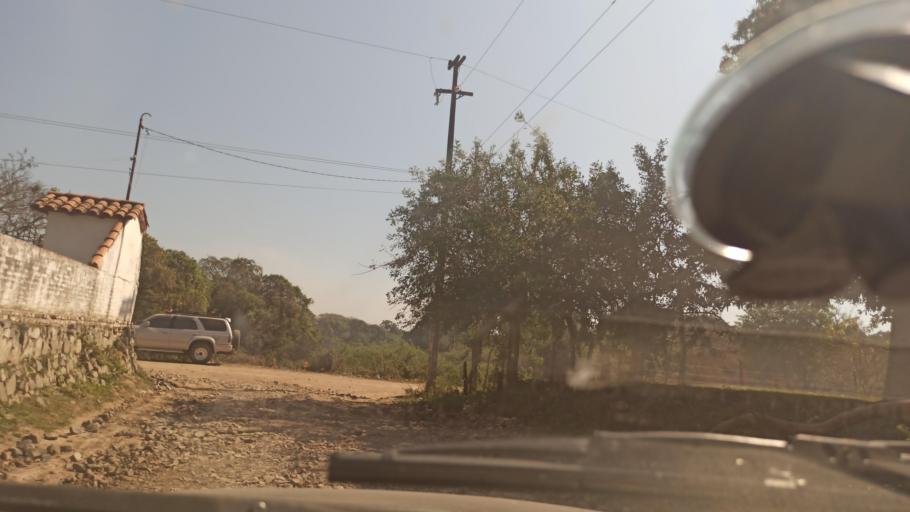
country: AR
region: Formosa
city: Clorinda
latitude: -25.3043
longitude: -57.6988
